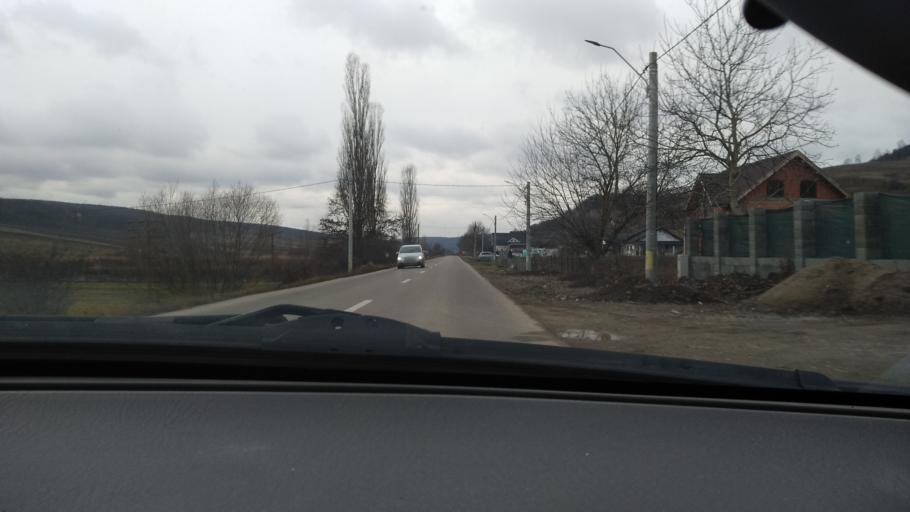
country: RO
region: Mures
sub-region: Comuna Livezeni
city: Livezeni
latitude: 46.5443
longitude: 24.6621
